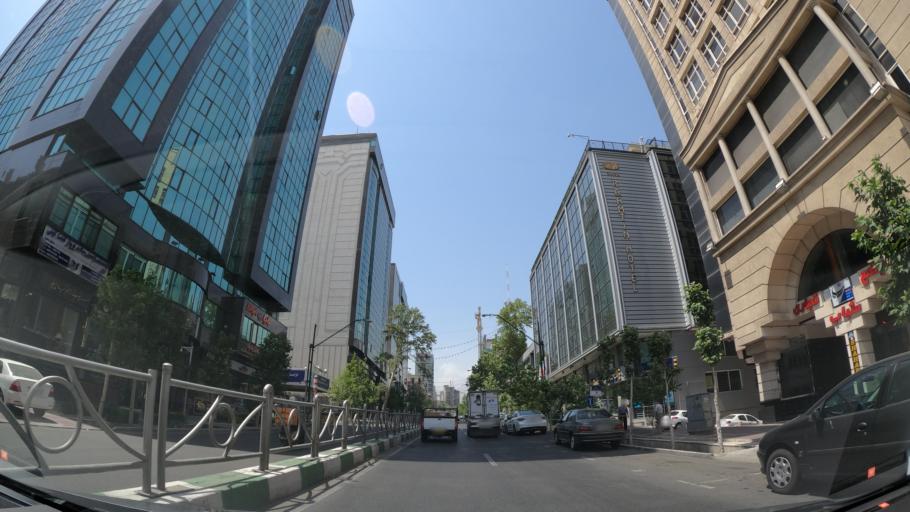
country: IR
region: Tehran
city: Tehran
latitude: 35.7319
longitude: 51.4114
